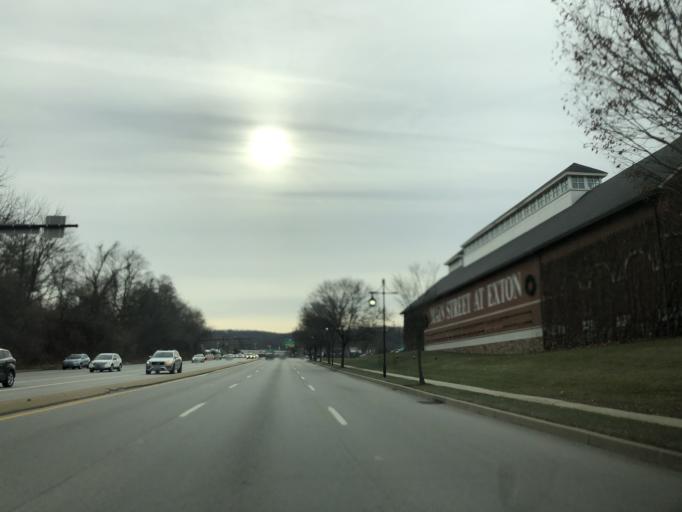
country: US
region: Pennsylvania
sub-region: Chester County
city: Exton
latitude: 40.0252
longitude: -75.6266
